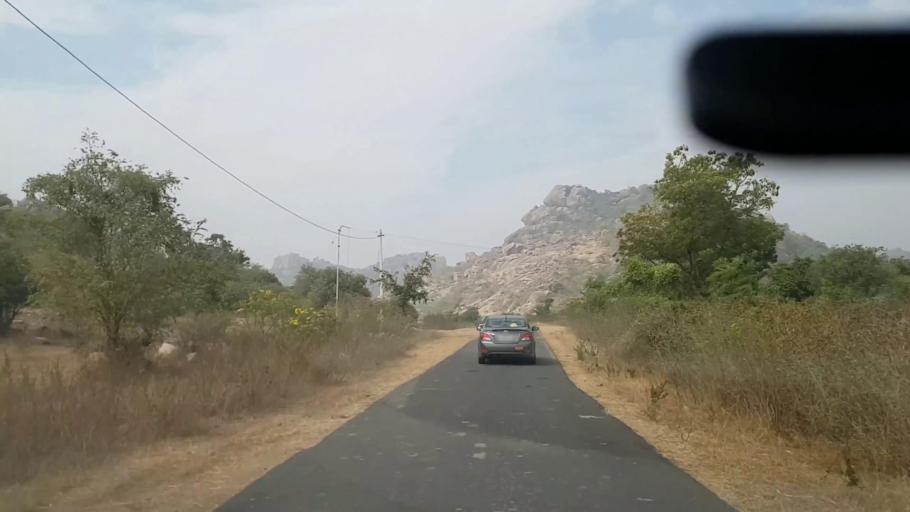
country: IN
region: Telangana
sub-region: Rangareddi
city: Ghatkesar
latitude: 17.1721
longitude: 78.8151
